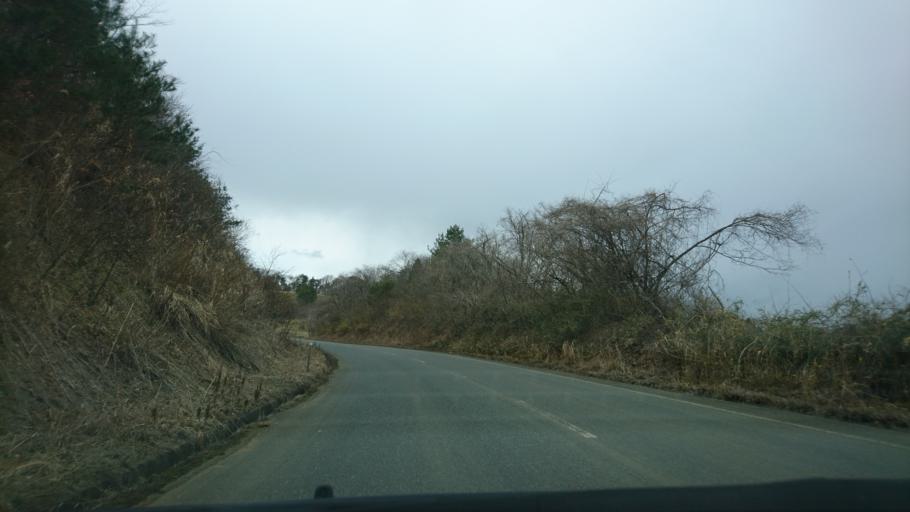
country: JP
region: Iwate
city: Ichinoseki
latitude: 38.8496
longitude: 141.2111
